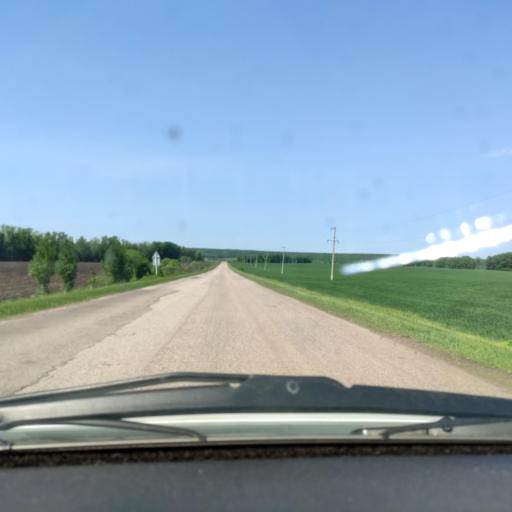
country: RU
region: Bashkortostan
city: Chishmy
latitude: 54.4618
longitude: 55.5406
